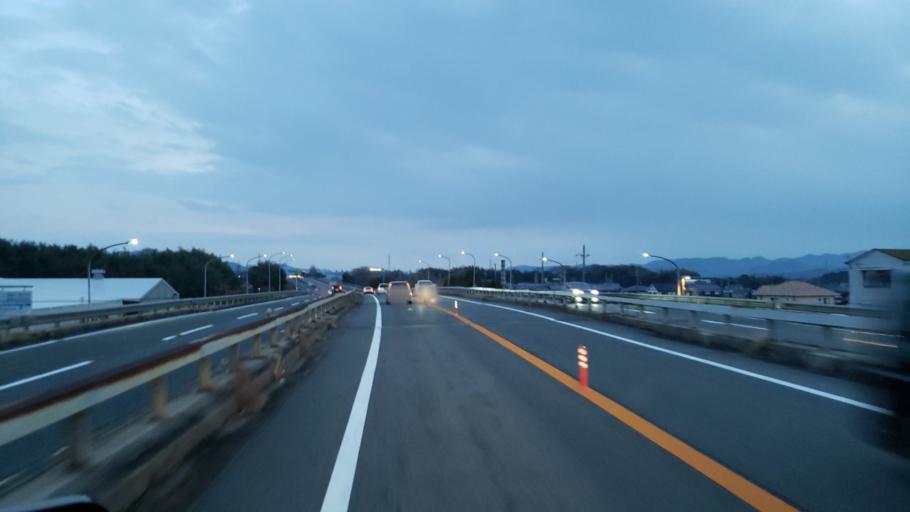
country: JP
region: Hyogo
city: Himeji
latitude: 34.9425
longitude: 134.7611
